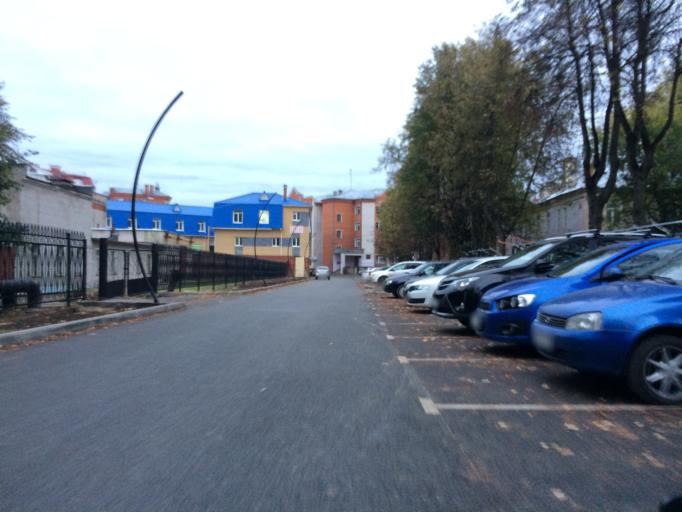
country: RU
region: Mariy-El
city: Yoshkar-Ola
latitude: 56.6372
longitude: 47.8776
